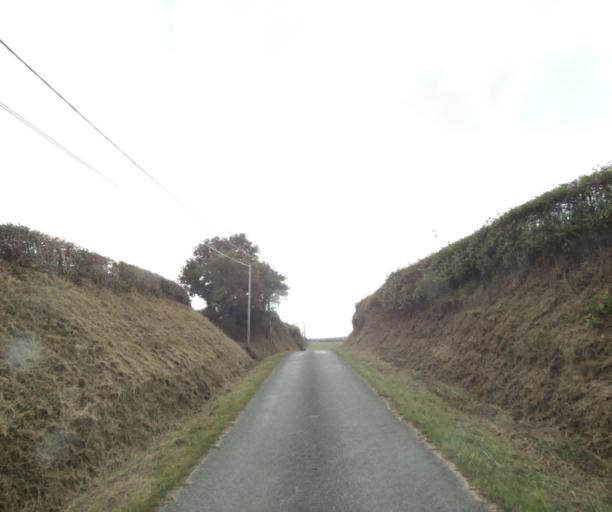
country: FR
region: Bourgogne
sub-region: Departement de Saone-et-Loire
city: Palinges
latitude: 46.4895
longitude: 4.2106
